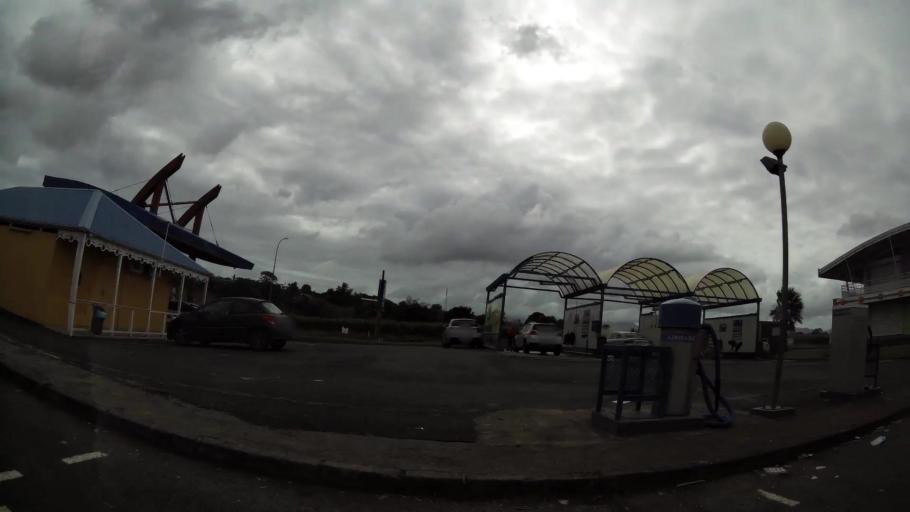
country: GP
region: Guadeloupe
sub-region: Guadeloupe
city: Lamentin
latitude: 16.2606
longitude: -61.6232
